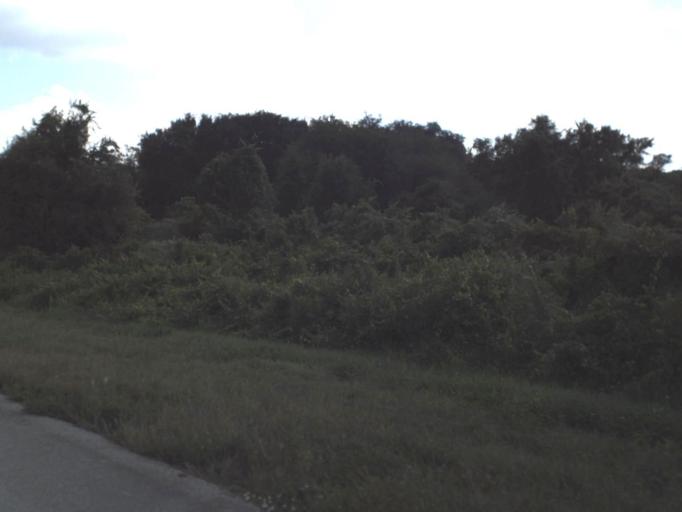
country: US
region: Florida
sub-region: Highlands County
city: Lake Placid
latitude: 27.4015
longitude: -81.1672
